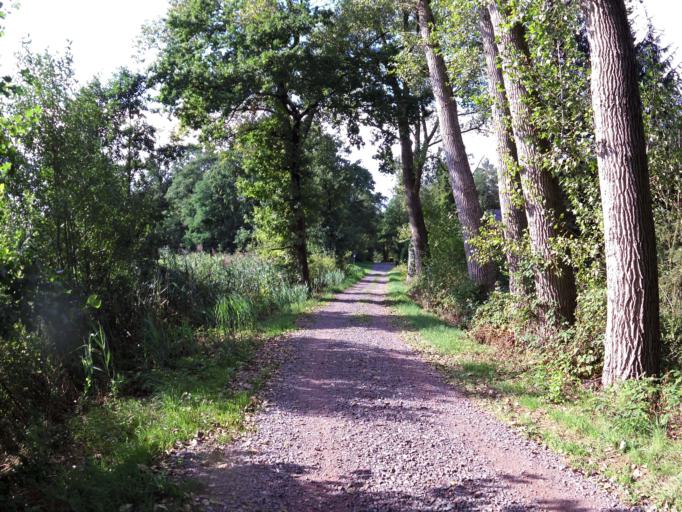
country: DE
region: Lower Saxony
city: Bremervorde
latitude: 53.4700
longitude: 9.1441
